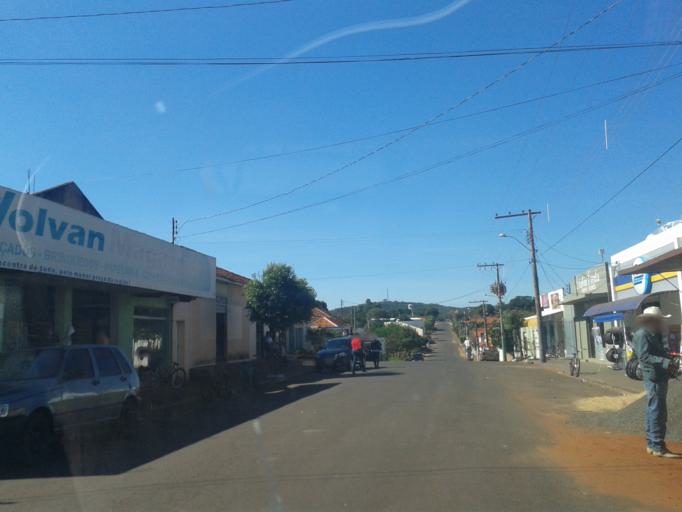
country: BR
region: Minas Gerais
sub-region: Ituiutaba
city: Ituiutaba
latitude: -19.2146
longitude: -49.7862
